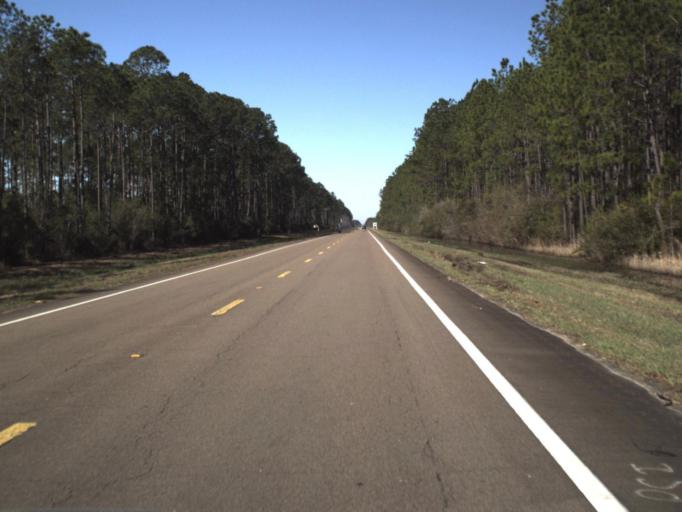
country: US
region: Florida
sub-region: Gulf County
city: Wewahitchka
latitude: 30.1378
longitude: -85.3845
